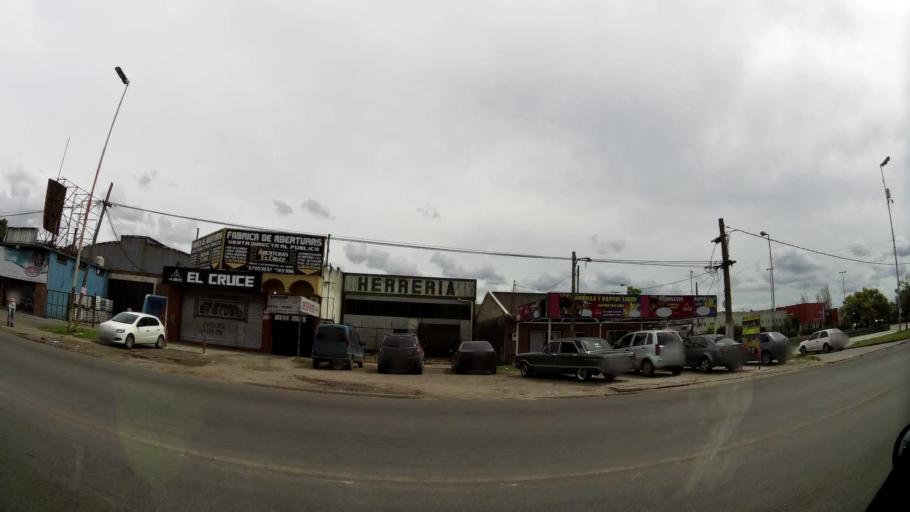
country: AR
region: Buenos Aires
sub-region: Partido de Quilmes
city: Quilmes
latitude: -34.7722
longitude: -58.2688
